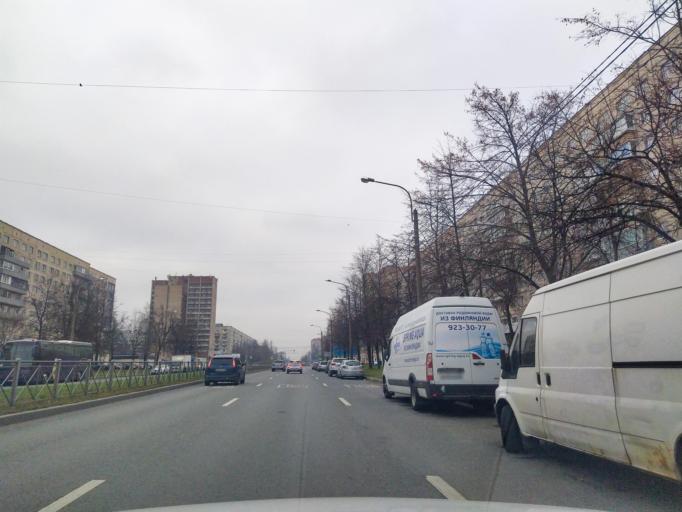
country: RU
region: St.-Petersburg
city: Sosnovka
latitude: 60.0380
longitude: 30.3456
